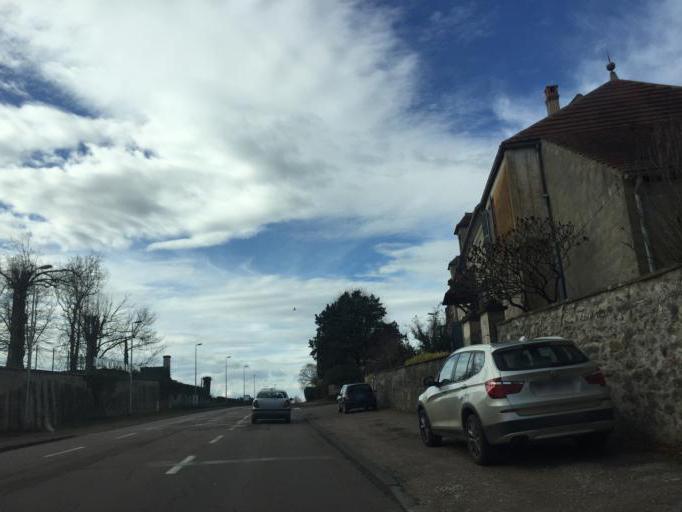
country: FR
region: Bourgogne
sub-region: Departement de l'Yonne
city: Avallon
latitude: 47.4948
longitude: 3.9031
